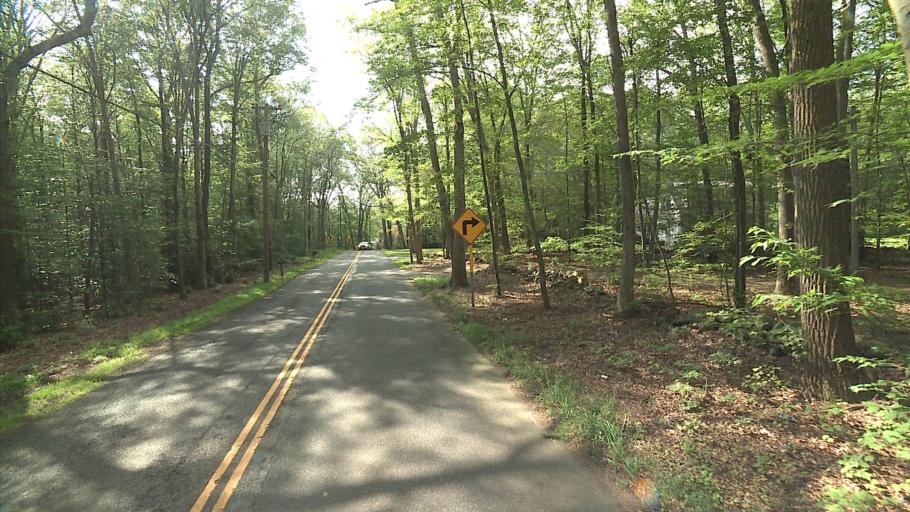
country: US
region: Connecticut
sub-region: Middlesex County
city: Chester Center
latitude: 41.3684
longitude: -72.4964
